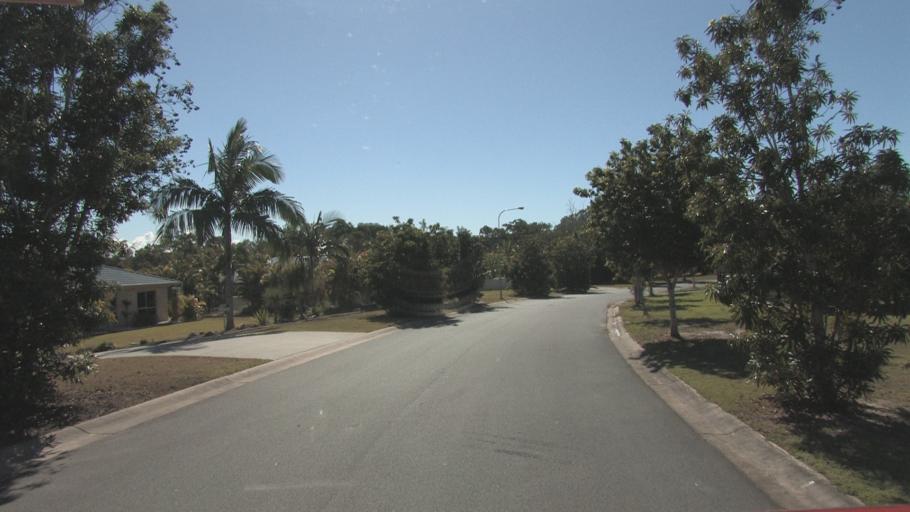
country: AU
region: Queensland
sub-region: Logan
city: Park Ridge South
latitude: -27.6869
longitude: 153.0075
